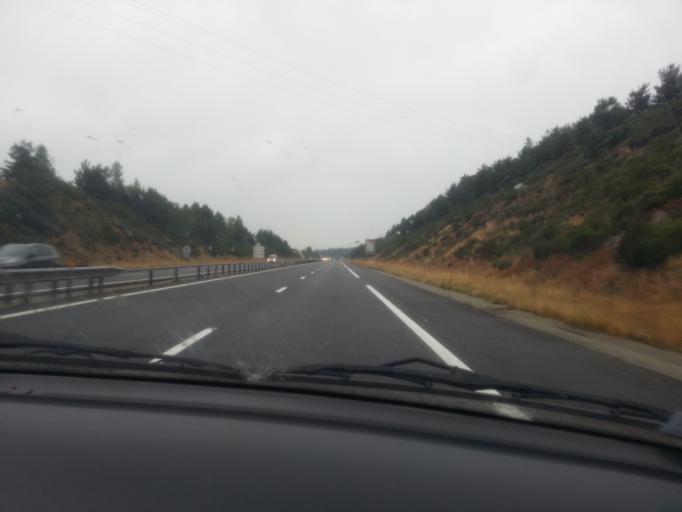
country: FR
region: Languedoc-Roussillon
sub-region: Departement de la Lozere
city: Aumont-Aubrac
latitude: 44.7541
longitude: 3.2885
